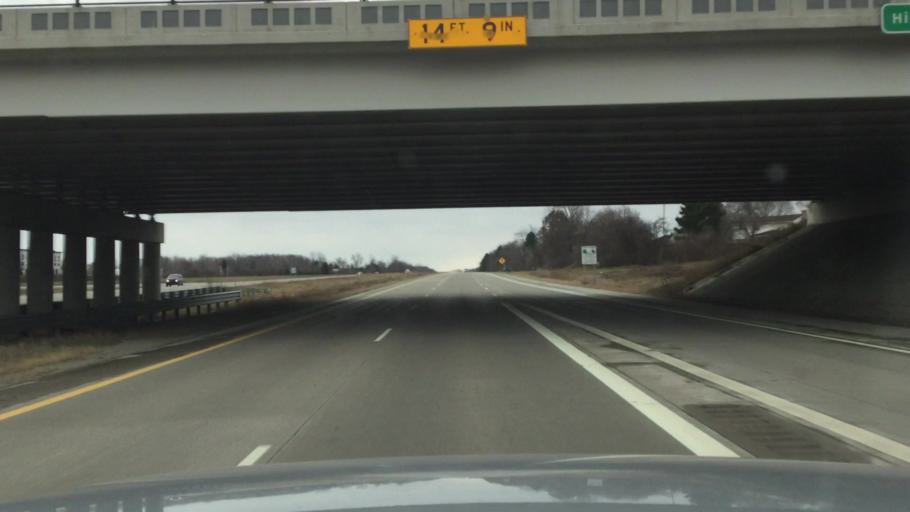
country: US
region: Michigan
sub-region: Genesee County
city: Grand Blanc
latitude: 42.9443
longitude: -83.6818
